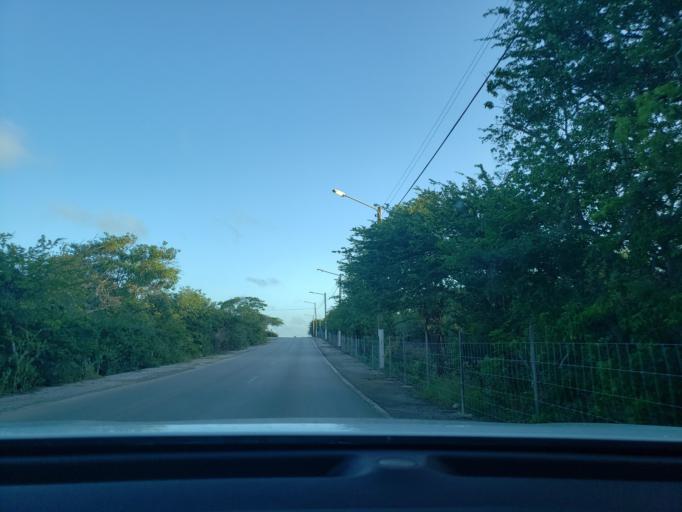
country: CW
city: Barber
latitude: 12.2680
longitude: -69.0653
